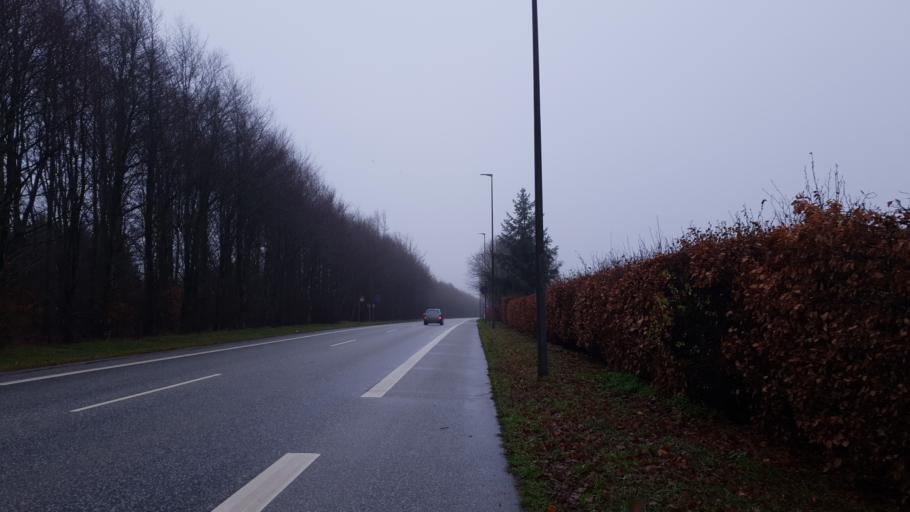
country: DK
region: Central Jutland
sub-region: Hedensted Kommune
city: Hedensted
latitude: 55.7930
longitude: 9.6996
